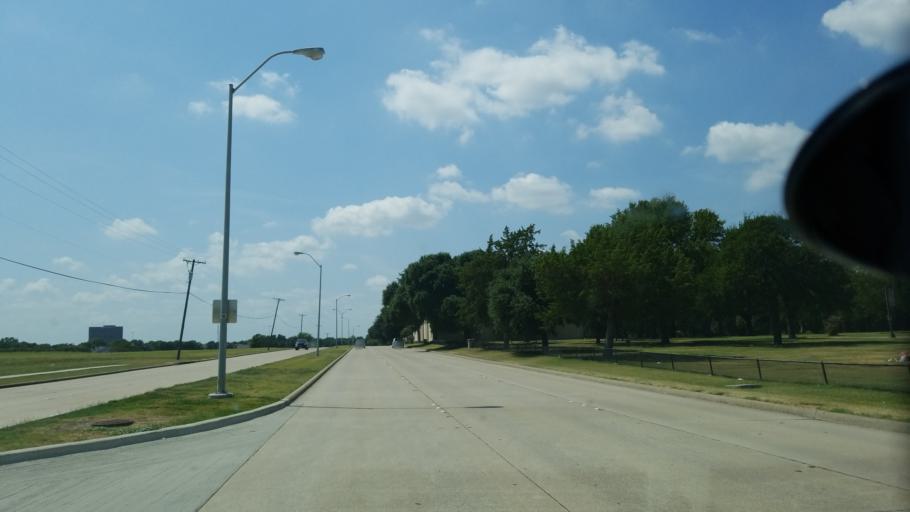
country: US
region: Texas
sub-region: Dallas County
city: Richardson
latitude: 32.9279
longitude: -96.7383
